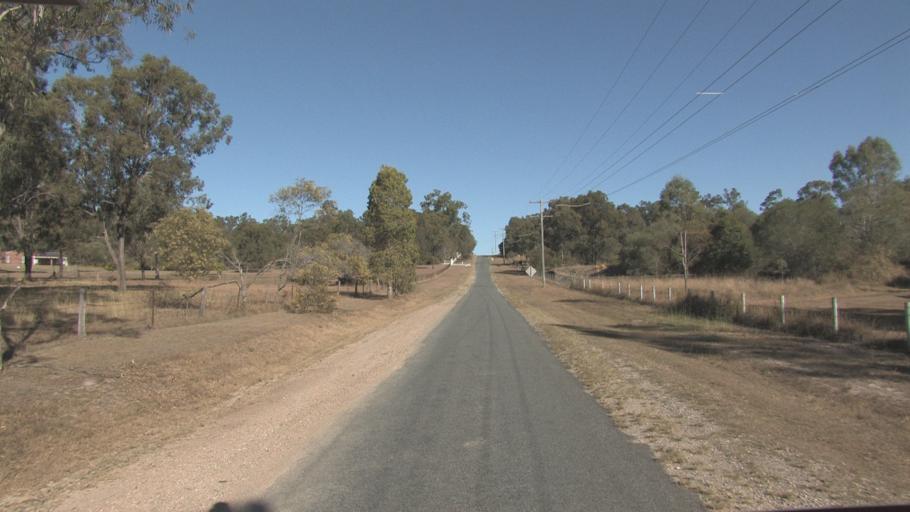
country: AU
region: Queensland
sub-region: Logan
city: Cedar Vale
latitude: -27.8577
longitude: 153.0274
